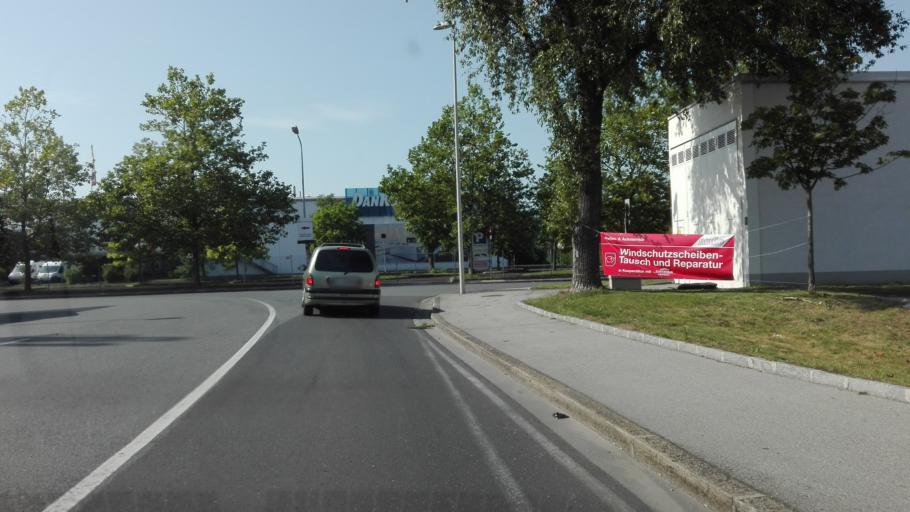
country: AT
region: Upper Austria
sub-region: Politischer Bezirk Linz-Land
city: Leonding
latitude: 48.2544
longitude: 14.2821
